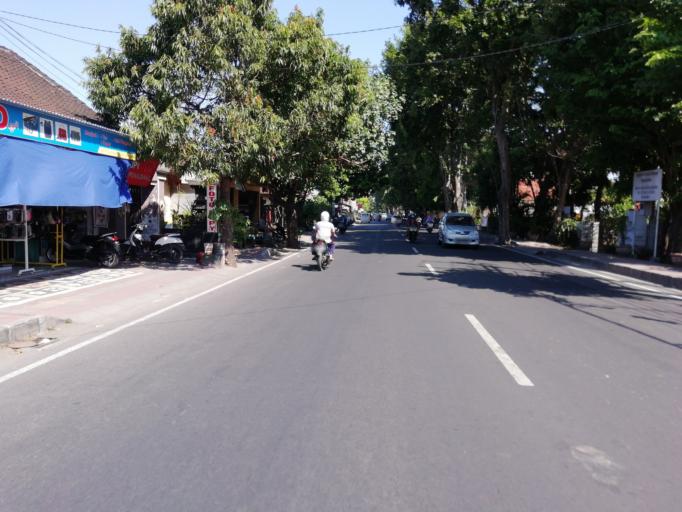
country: ID
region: Bali
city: Karyadharma
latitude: -8.7010
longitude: 115.2195
